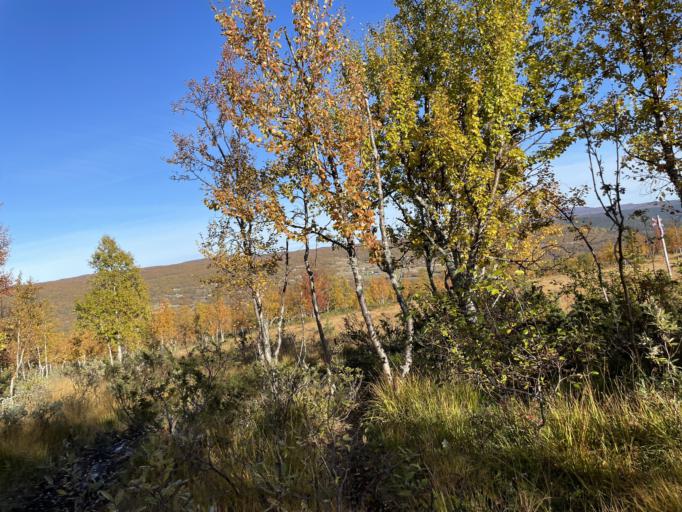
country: NO
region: Sor-Trondelag
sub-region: Tydal
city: Aas
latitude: 62.6389
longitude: 12.3909
